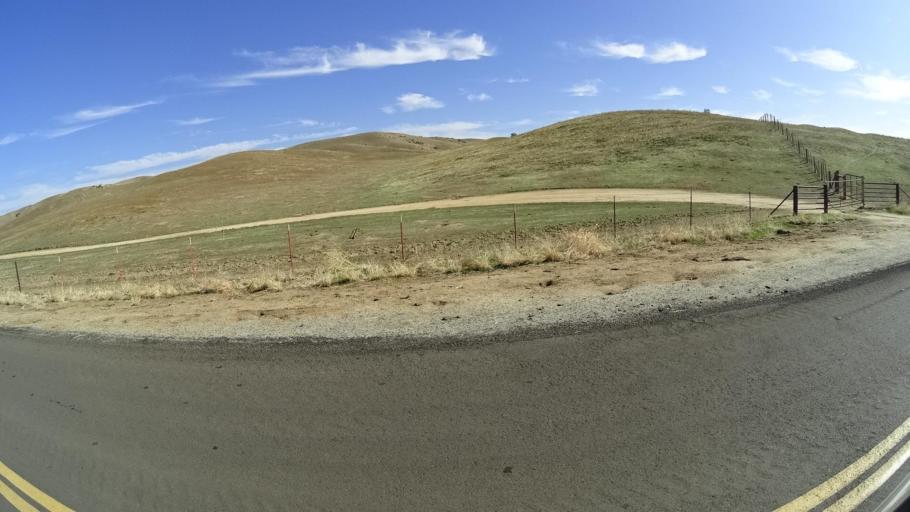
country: US
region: California
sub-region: Tulare County
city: Richgrove
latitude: 35.6777
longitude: -118.8948
